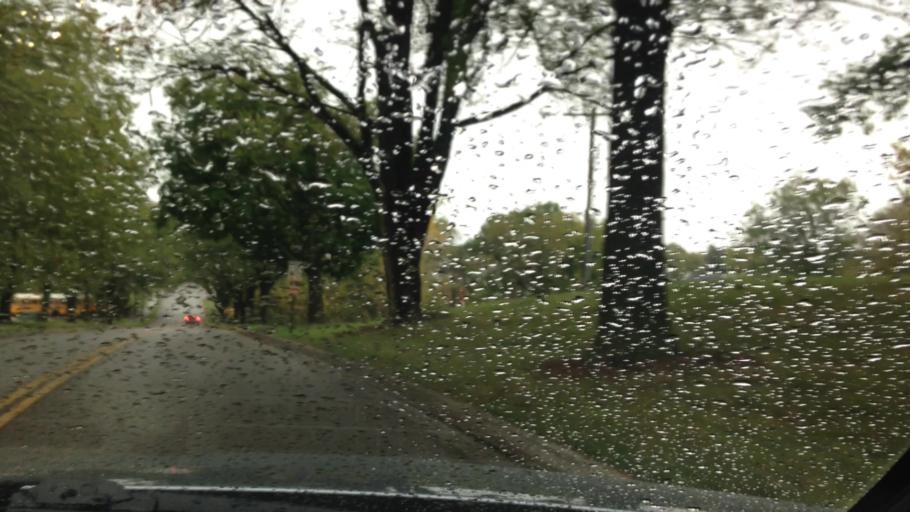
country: US
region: Kansas
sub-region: Leavenworth County
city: Leavenworth
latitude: 39.3408
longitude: -94.9327
